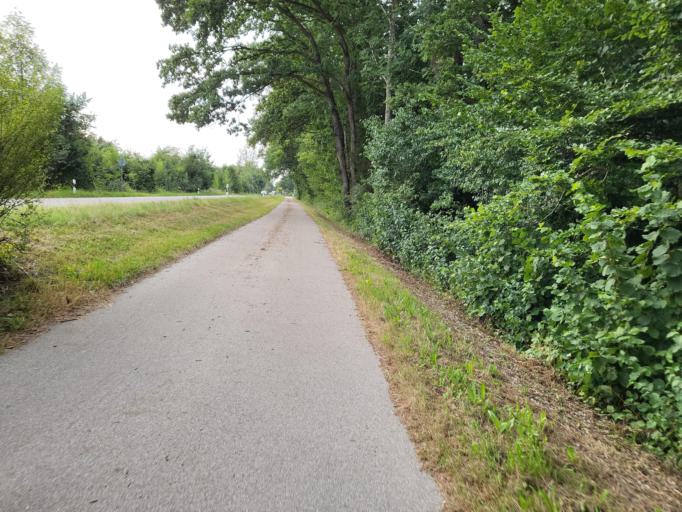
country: DE
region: Bavaria
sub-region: Upper Bavaria
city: Hohenkirchen-Siegertsbrunn
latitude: 48.0110
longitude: 11.7202
